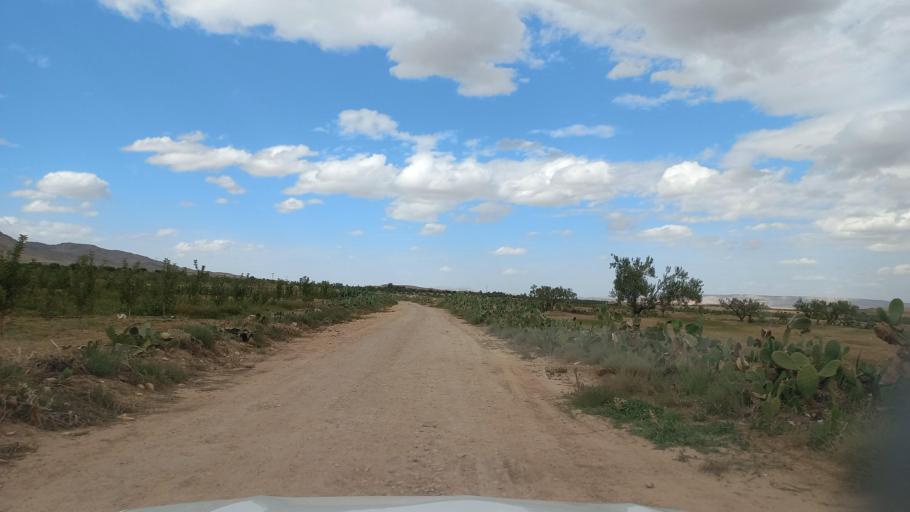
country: TN
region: Al Qasrayn
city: Sbiba
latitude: 35.4332
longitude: 9.0978
